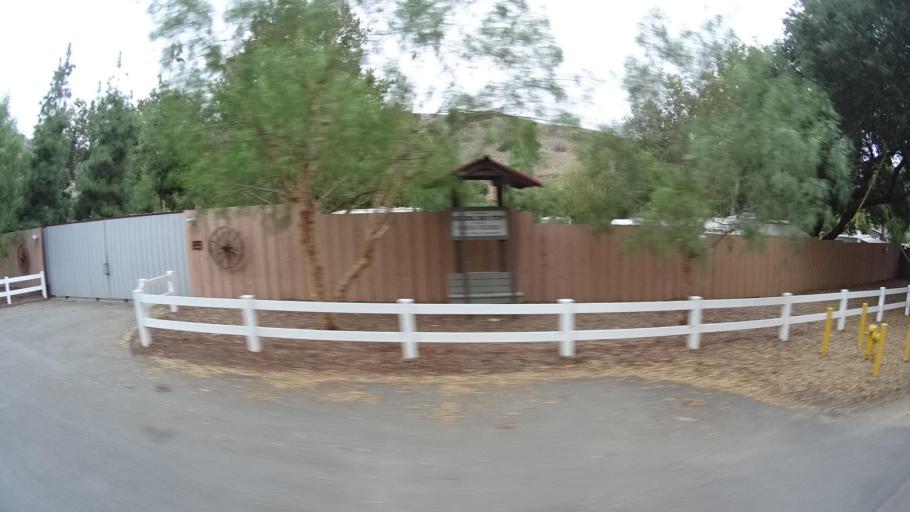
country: US
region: California
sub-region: San Diego County
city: Crest
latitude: 32.8011
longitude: -116.8451
